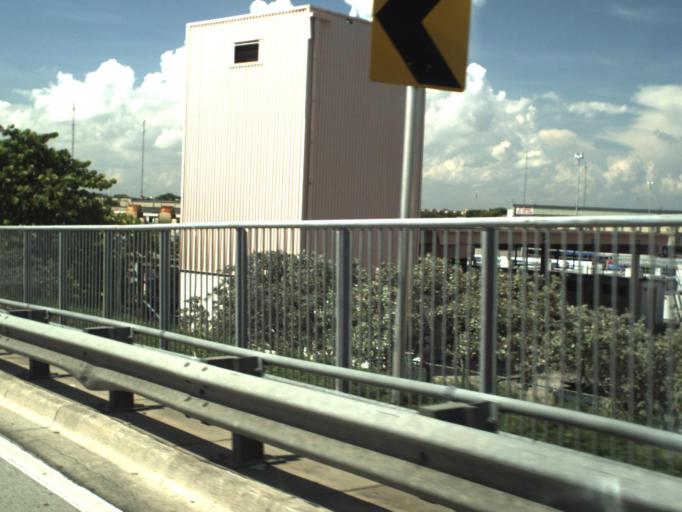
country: US
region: Florida
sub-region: Miami-Dade County
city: Norland
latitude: 25.9425
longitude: -80.1941
